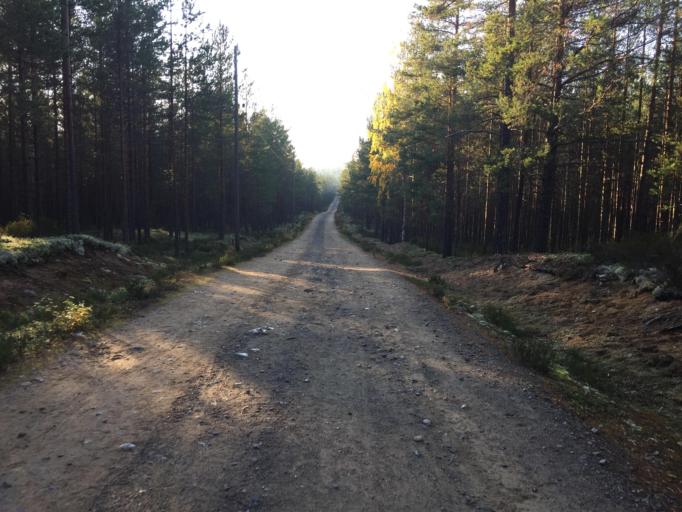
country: RU
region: Leningrad
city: Priozersk
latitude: 61.2837
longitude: 30.1184
